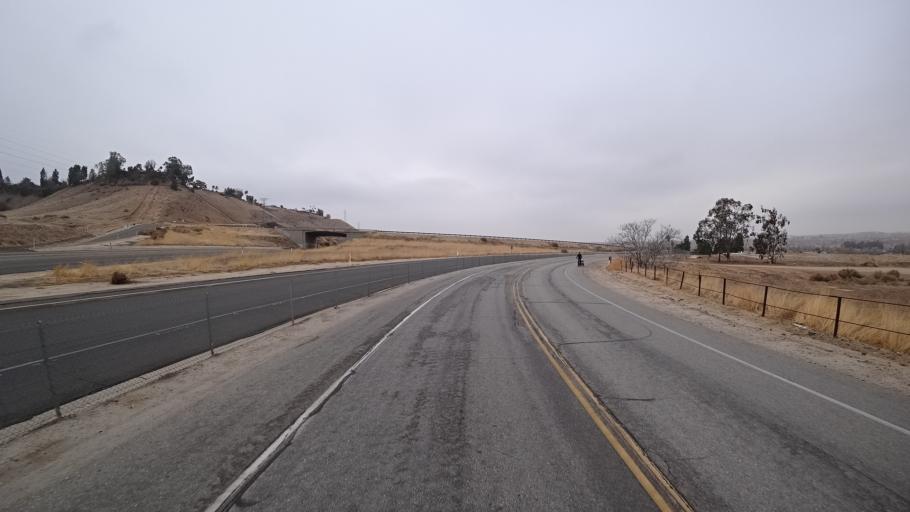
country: US
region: California
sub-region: Kern County
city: Oildale
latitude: 35.4176
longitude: -118.9581
